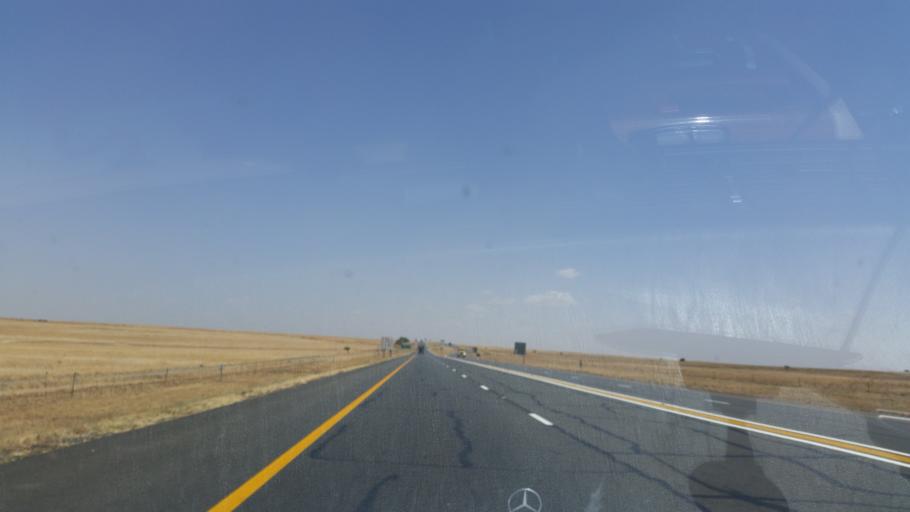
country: ZA
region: Orange Free State
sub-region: Lejweleputswa District Municipality
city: Brandfort
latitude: -28.8780
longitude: 26.5050
